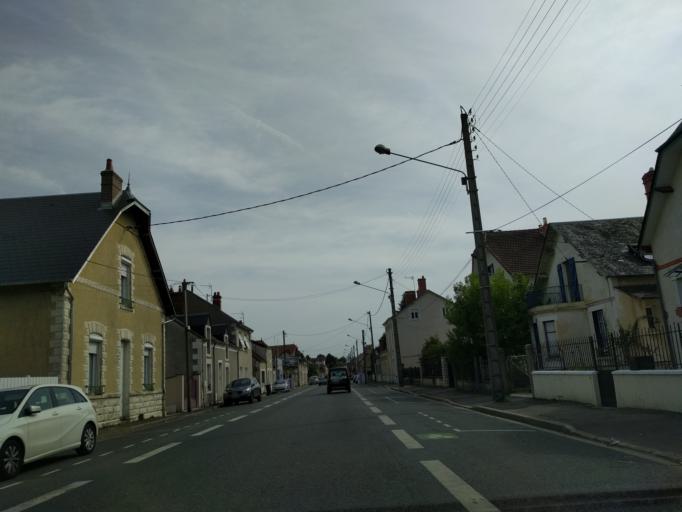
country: FR
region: Centre
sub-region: Departement du Cher
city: Bourges
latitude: 47.0666
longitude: 2.4177
